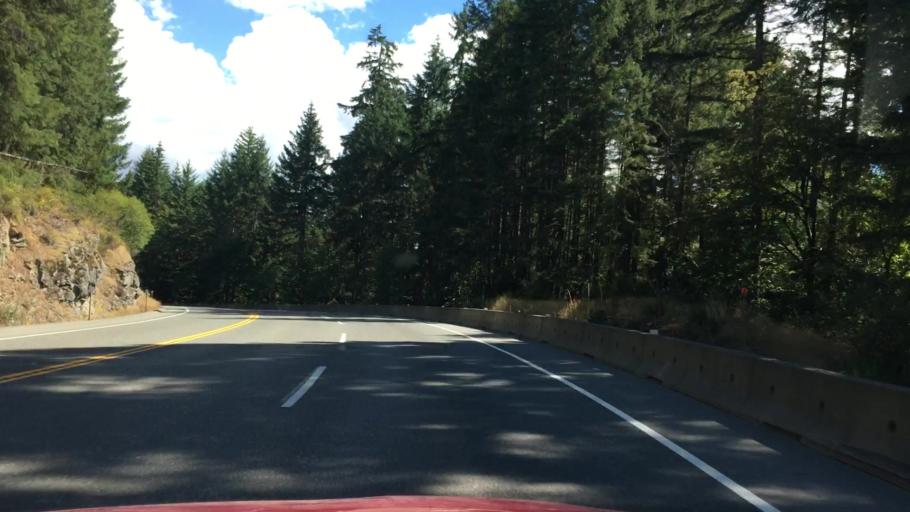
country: CA
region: British Columbia
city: Port Alberni
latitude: 49.2651
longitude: -124.7310
